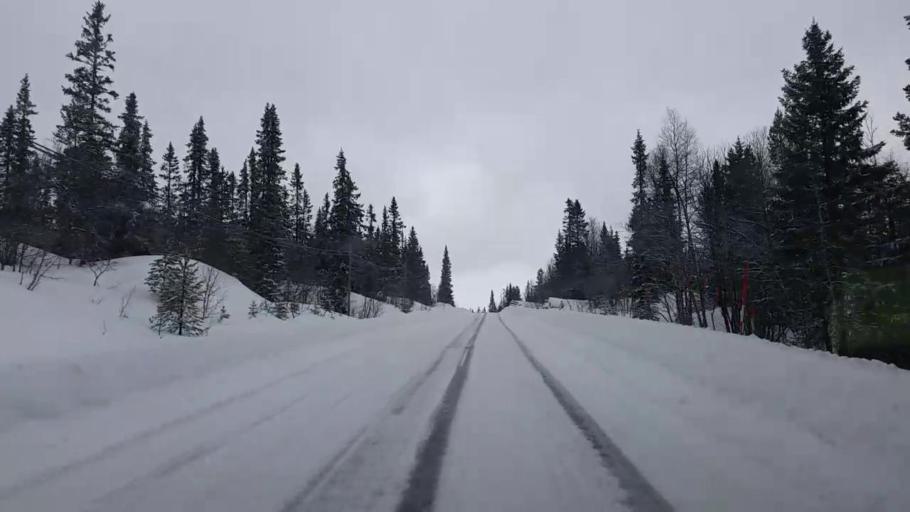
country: SE
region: Jaemtland
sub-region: Bergs Kommun
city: Hoverberg
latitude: 62.4897
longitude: 14.1179
